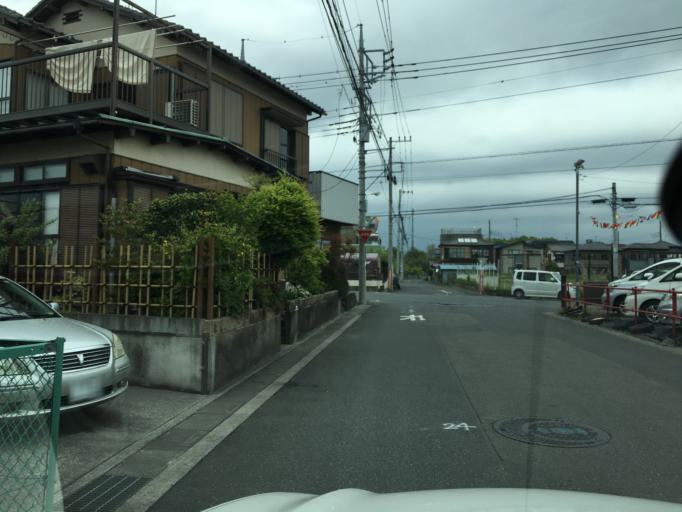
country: JP
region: Saitama
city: Yoshikawa
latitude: 35.8880
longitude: 139.8245
